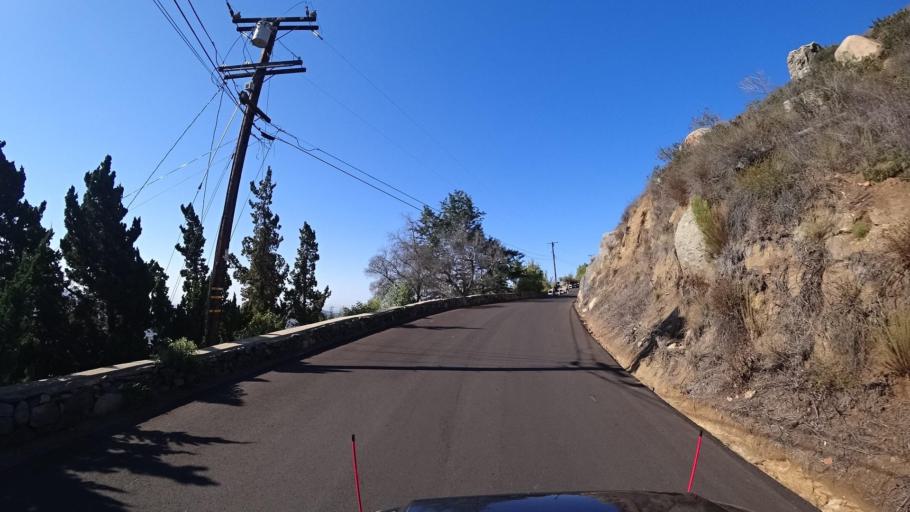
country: US
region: California
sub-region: San Diego County
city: Casa de Oro-Mount Helix
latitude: 32.7667
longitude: -116.9815
